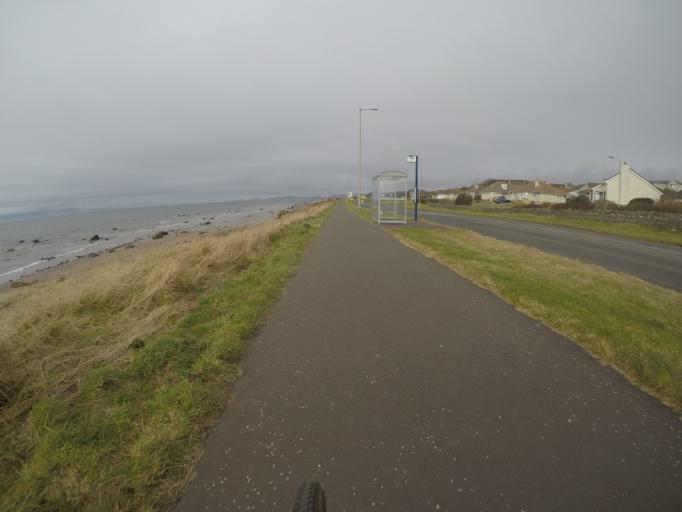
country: GB
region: Scotland
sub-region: North Ayrshire
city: Ardrossan
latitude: 55.6534
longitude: -4.8233
